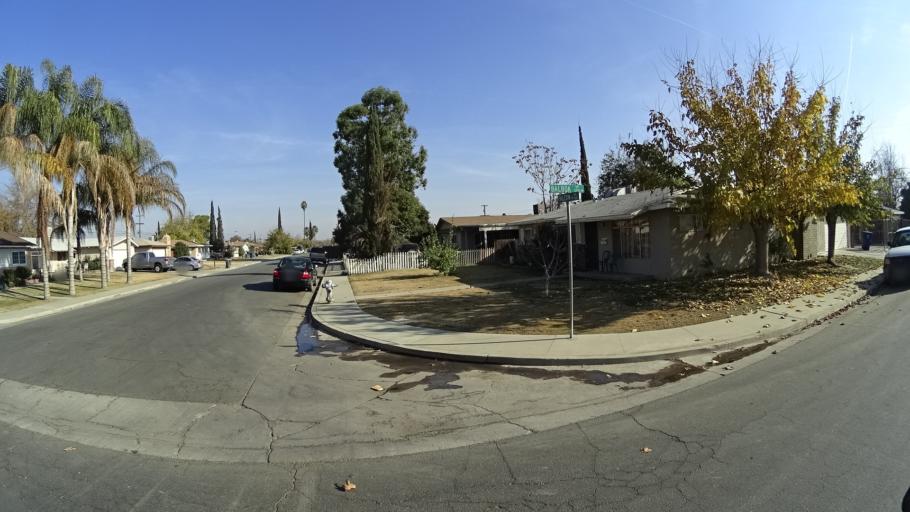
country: US
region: California
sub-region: Kern County
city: Bakersfield
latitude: 35.3208
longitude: -119.0203
